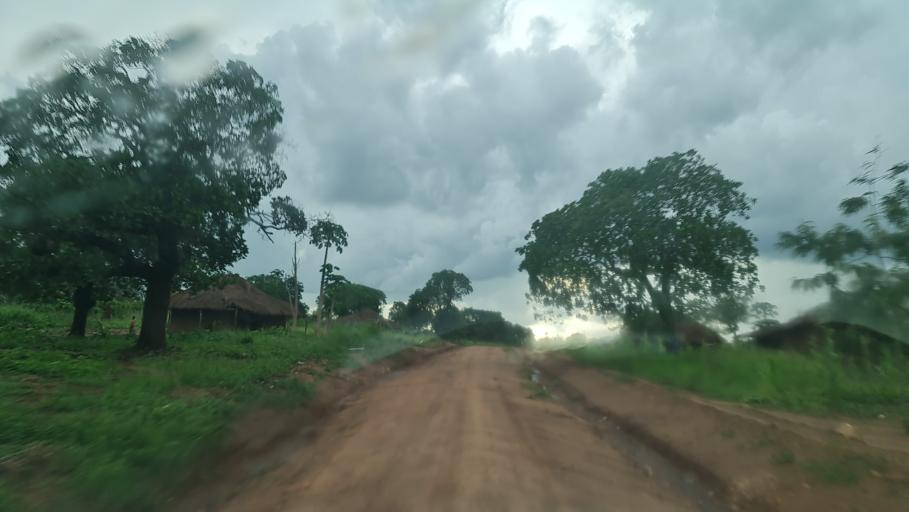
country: MZ
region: Nampula
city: Nacala
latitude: -13.9843
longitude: 40.4023
